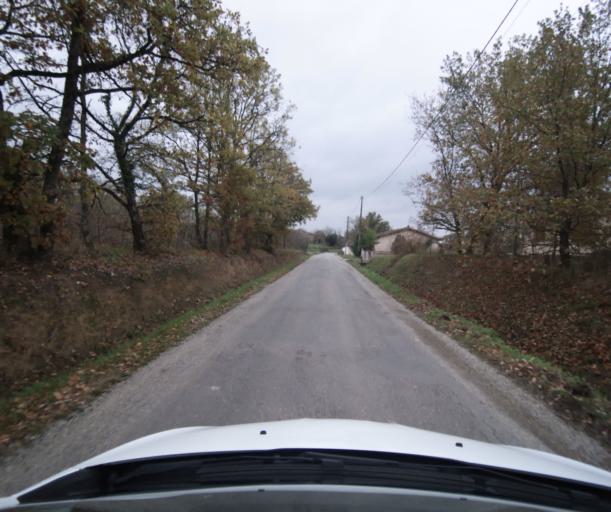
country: FR
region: Midi-Pyrenees
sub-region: Departement du Tarn-et-Garonne
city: Moissac
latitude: 44.0733
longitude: 1.1390
